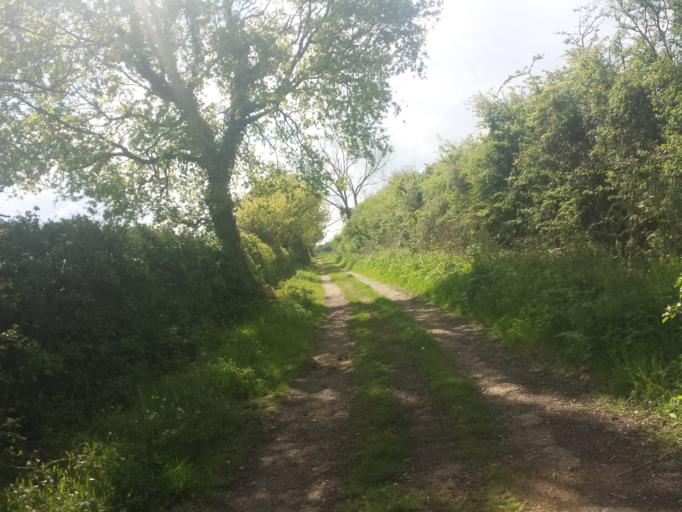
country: GB
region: England
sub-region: Essex
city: Great Bentley
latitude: 51.8805
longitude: 1.0446
